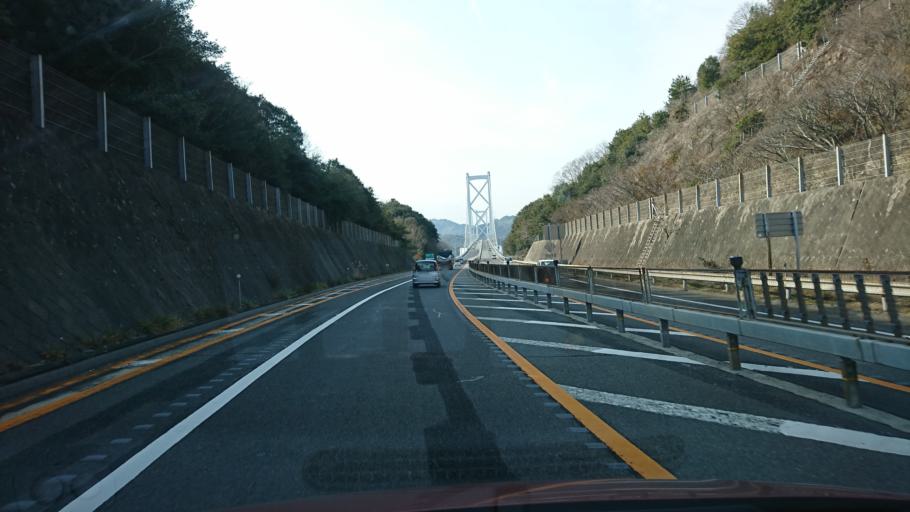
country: JP
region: Hiroshima
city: Onomichi
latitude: 34.3616
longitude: 133.1906
